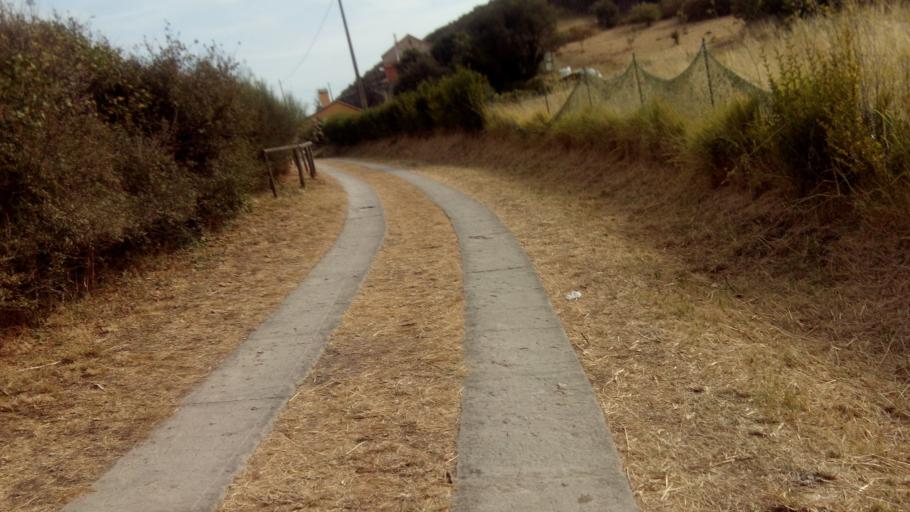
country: ES
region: Galicia
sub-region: Provincia de Pontevedra
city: Sanxenxo
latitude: 42.3686
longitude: -8.9349
